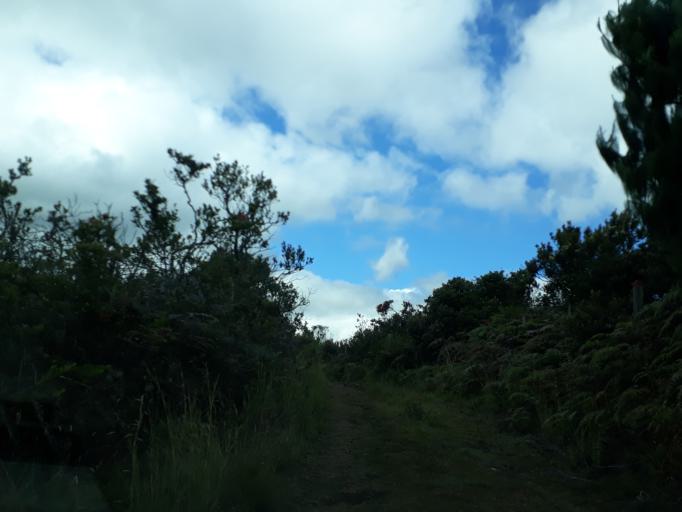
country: CO
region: Cundinamarca
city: Guacheta
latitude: 5.4464
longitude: -73.6944
